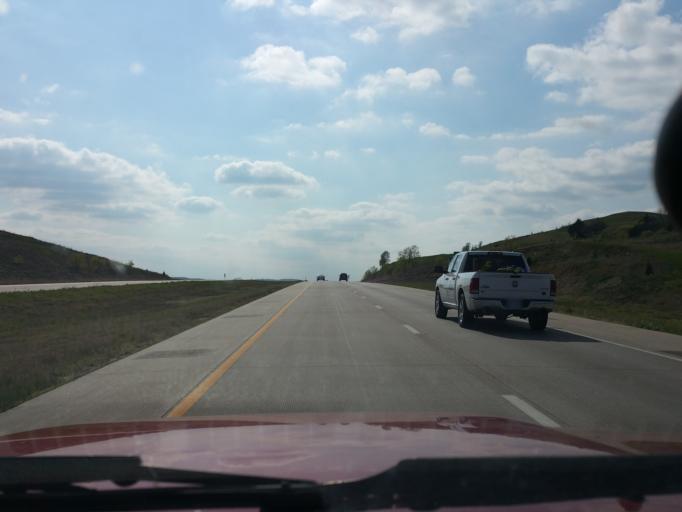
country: US
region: Kansas
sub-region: Pottawatomie County
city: Saint Marys
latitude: 39.0591
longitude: -96.0718
